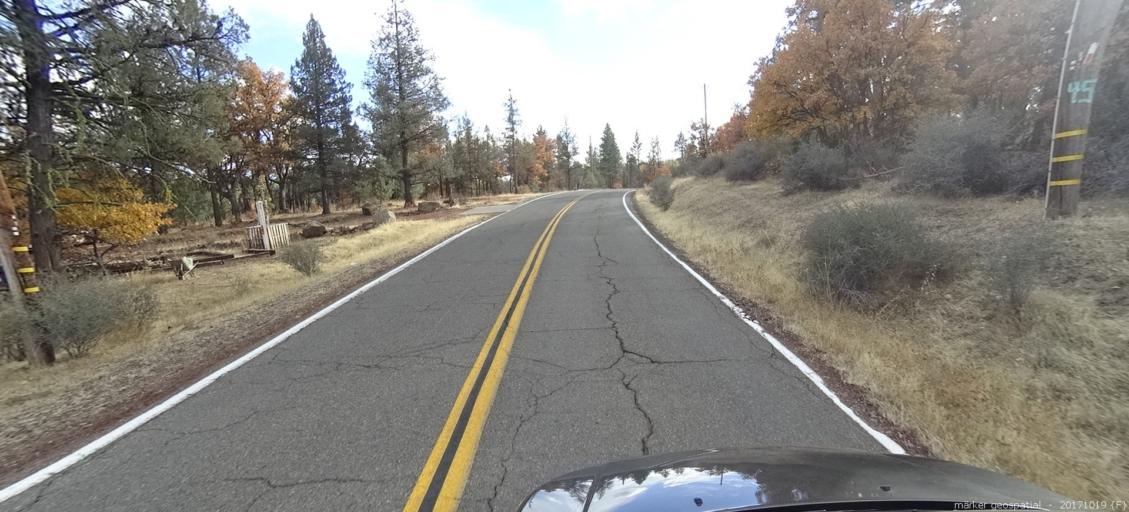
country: US
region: California
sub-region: Shasta County
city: Burney
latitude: 40.9702
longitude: -121.4330
